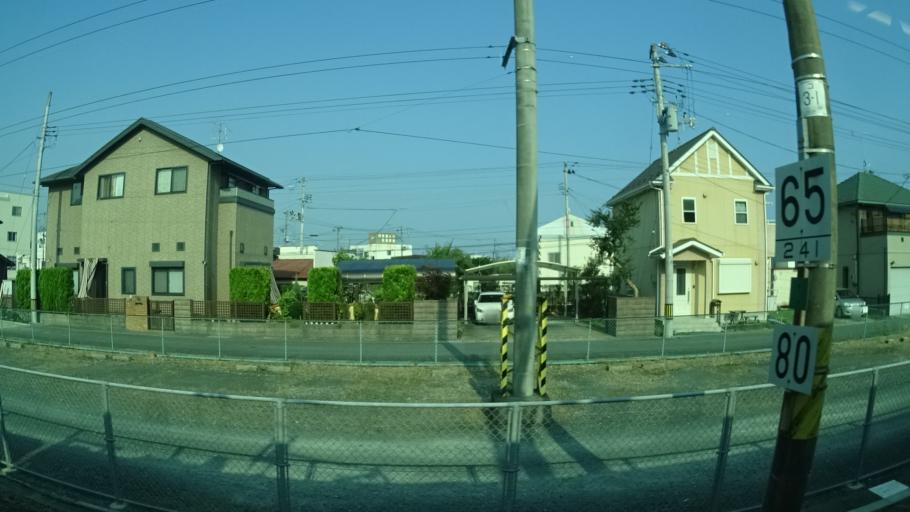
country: JP
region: Ibaraki
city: Kitaibaraki
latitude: 36.9195
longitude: 140.7966
